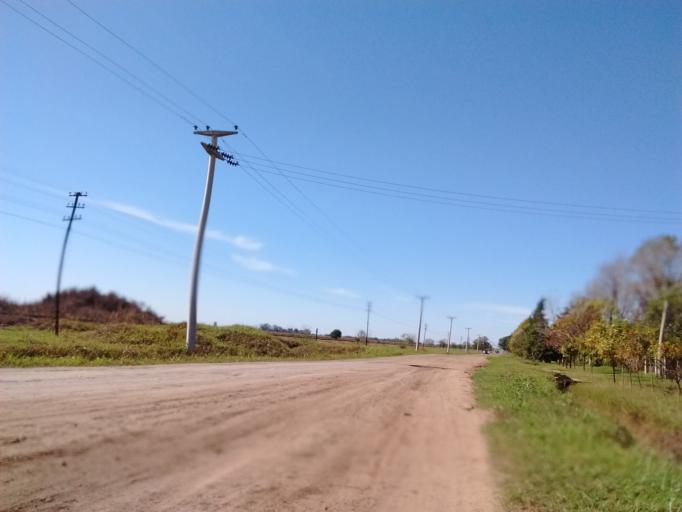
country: AR
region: Santa Fe
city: Funes
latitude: -32.9103
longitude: -60.8494
